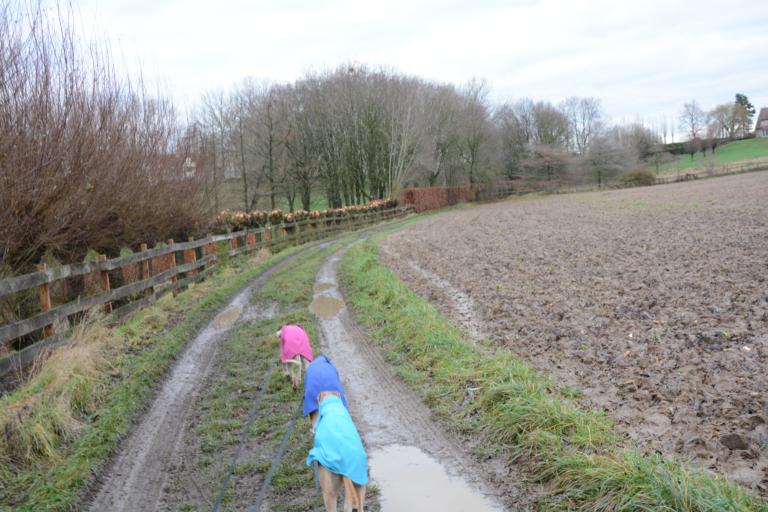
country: BE
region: Flanders
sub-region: Provincie Vlaams-Brabant
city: Merchtem
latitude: 50.9294
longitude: 4.2483
